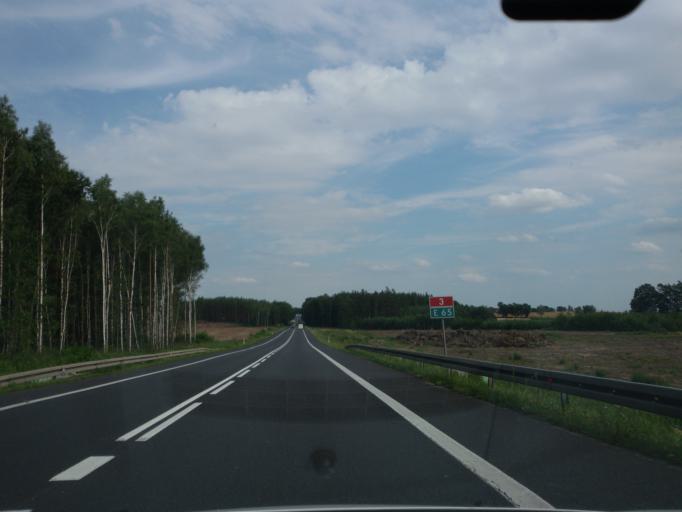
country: PL
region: Lower Silesian Voivodeship
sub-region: Powiat polkowicki
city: Gaworzyce
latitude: 51.6500
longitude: 15.8547
